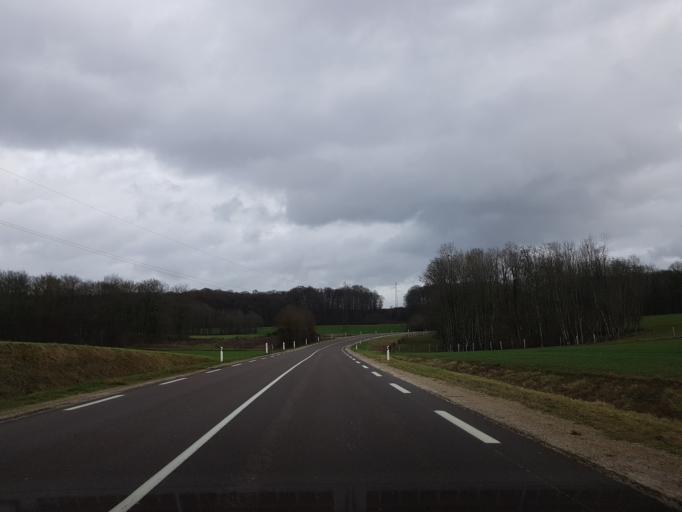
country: FR
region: Franche-Comte
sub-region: Departement de la Haute-Saone
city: Scey-sur-Saone-et-Saint-Albin
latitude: 47.7085
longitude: 5.9240
